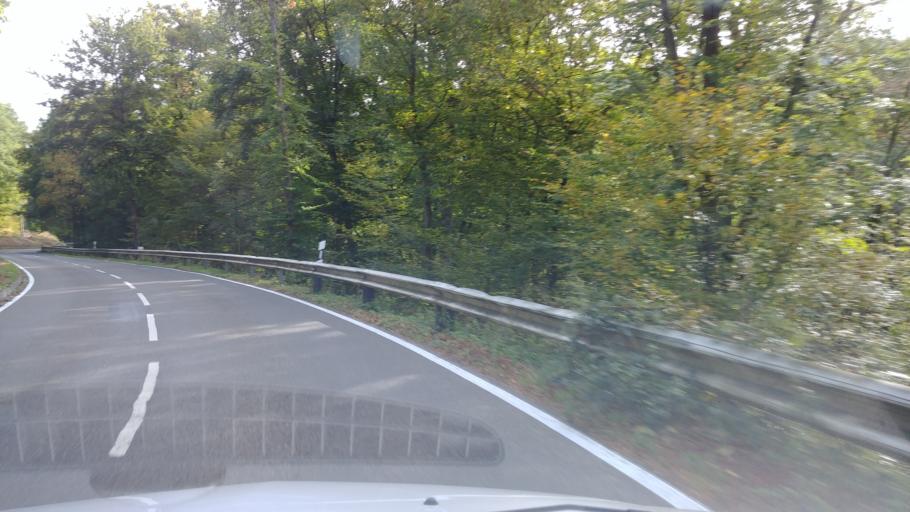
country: DE
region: Rheinland-Pfalz
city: Reckenroth
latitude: 50.2243
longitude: 8.0355
